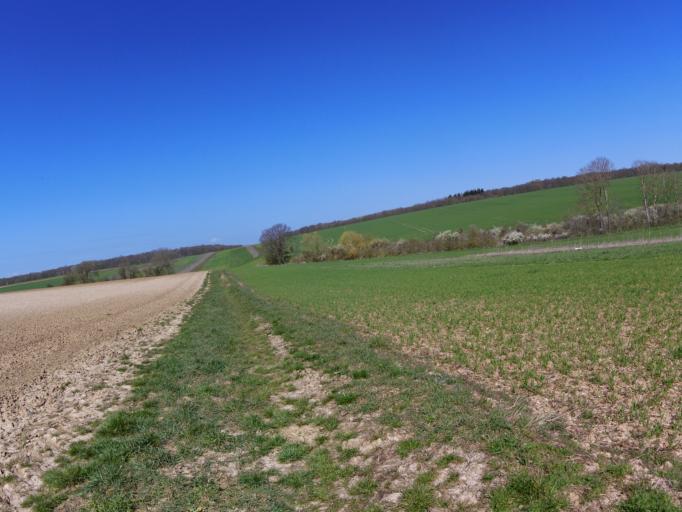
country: DE
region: Bavaria
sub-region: Regierungsbezirk Unterfranken
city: Rottendorf
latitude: 49.8027
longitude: 10.0346
